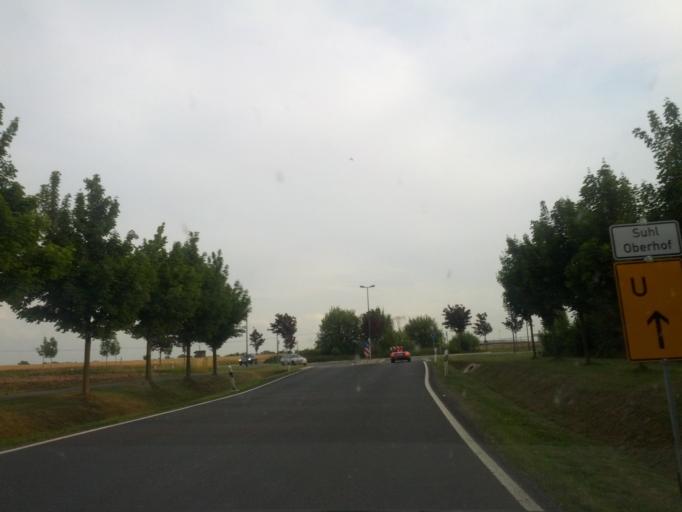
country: DE
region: Thuringia
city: Gotha
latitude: 50.9299
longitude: 10.6828
